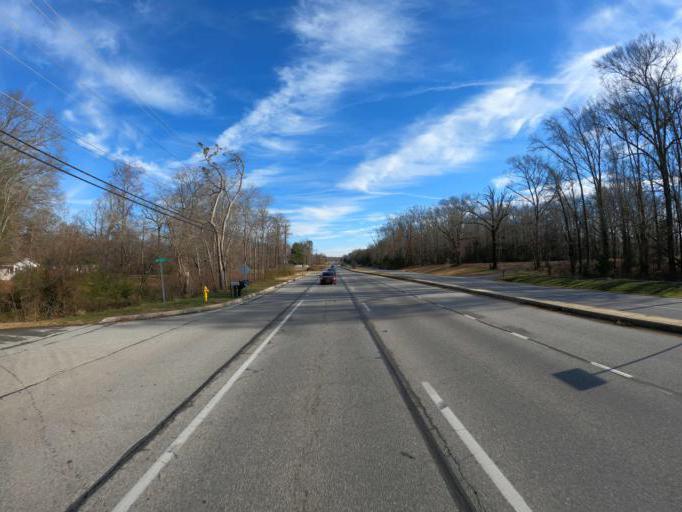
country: US
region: Maryland
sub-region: Charles County
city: Saint Charles
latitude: 38.6082
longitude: -76.9581
